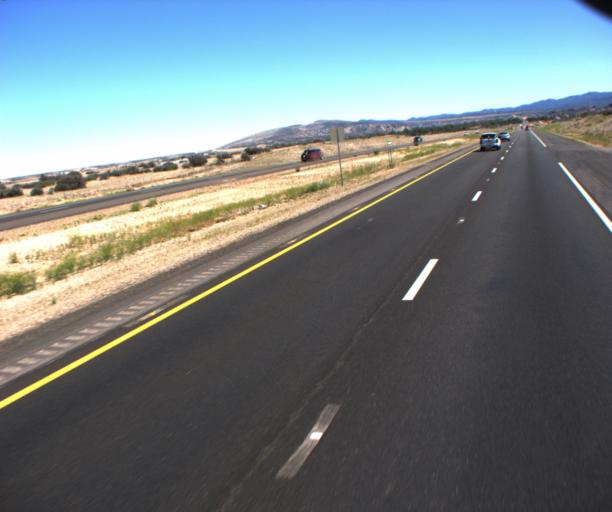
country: US
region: Arizona
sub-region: Yavapai County
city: Chino Valley
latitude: 34.6647
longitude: -112.4385
